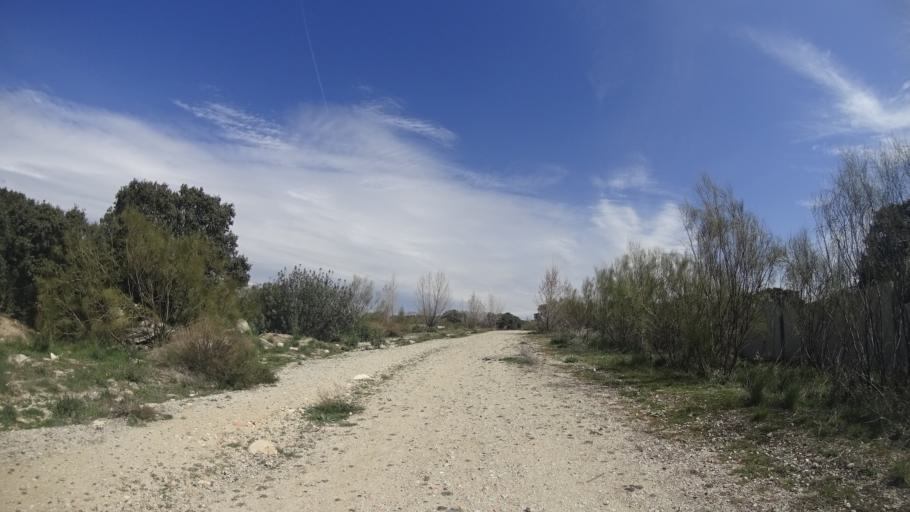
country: ES
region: Madrid
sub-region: Provincia de Madrid
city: Torrelodones
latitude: 40.5618
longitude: -3.9162
